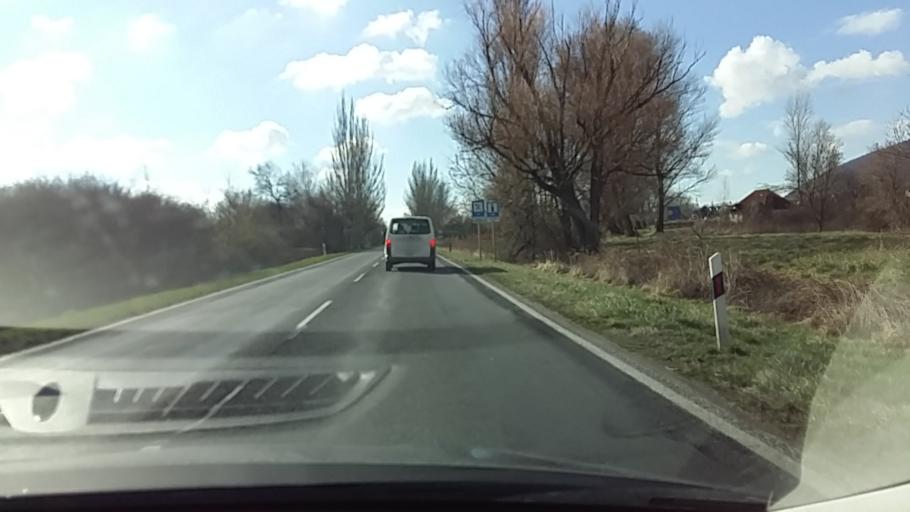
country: HU
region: Veszprem
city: Tapolca
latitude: 46.8211
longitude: 17.3809
